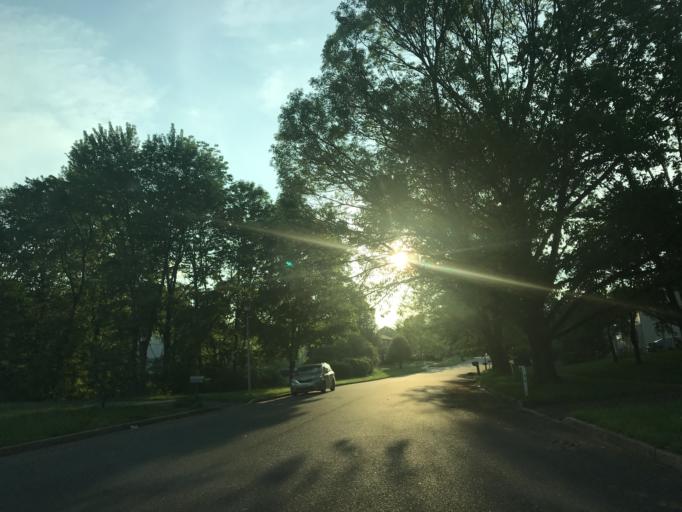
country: US
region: Maryland
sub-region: Harford County
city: Bel Air
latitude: 39.5411
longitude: -76.3431
